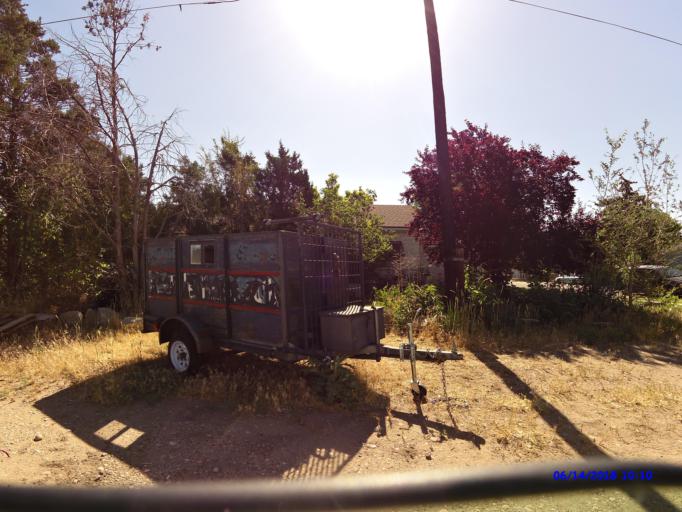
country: US
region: Utah
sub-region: Weber County
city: Ogden
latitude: 41.2242
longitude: -111.9955
